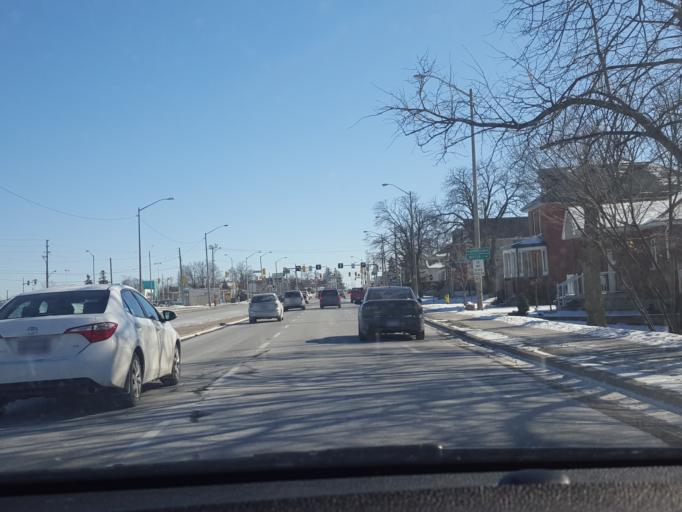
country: CA
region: Ontario
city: Cambridge
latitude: 43.3746
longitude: -80.3208
